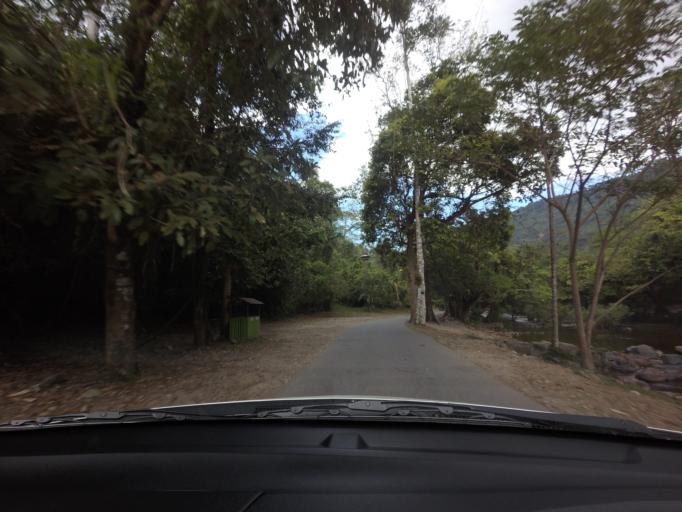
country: TH
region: Nakhon Nayok
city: Nakhon Nayok
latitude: 14.3309
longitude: 101.3047
